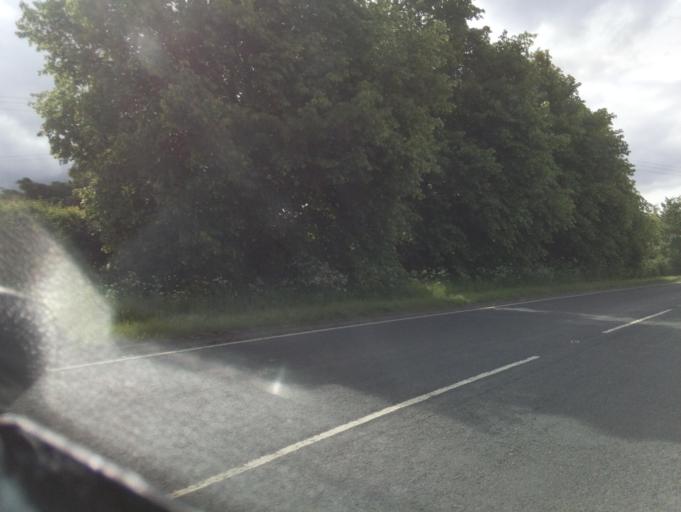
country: GB
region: England
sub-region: Worcestershire
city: Pershore
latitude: 52.1421
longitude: -2.1374
